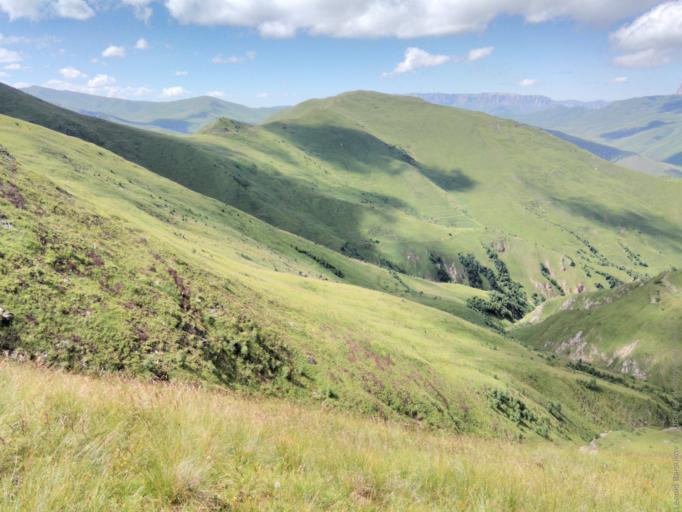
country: RU
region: Kabardino-Balkariya
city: Tyrnyauz
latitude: 43.4262
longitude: 42.8780
